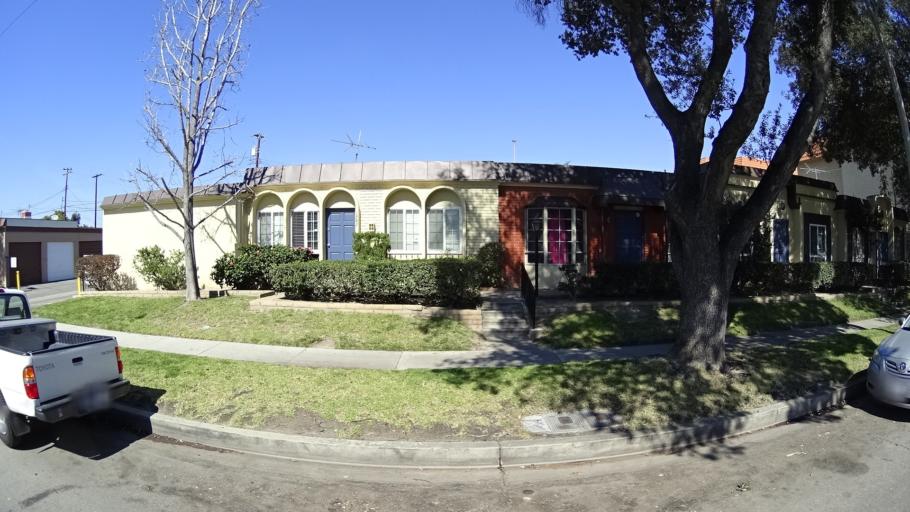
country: US
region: California
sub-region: Orange County
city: Anaheim
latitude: 33.8430
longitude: -117.9437
